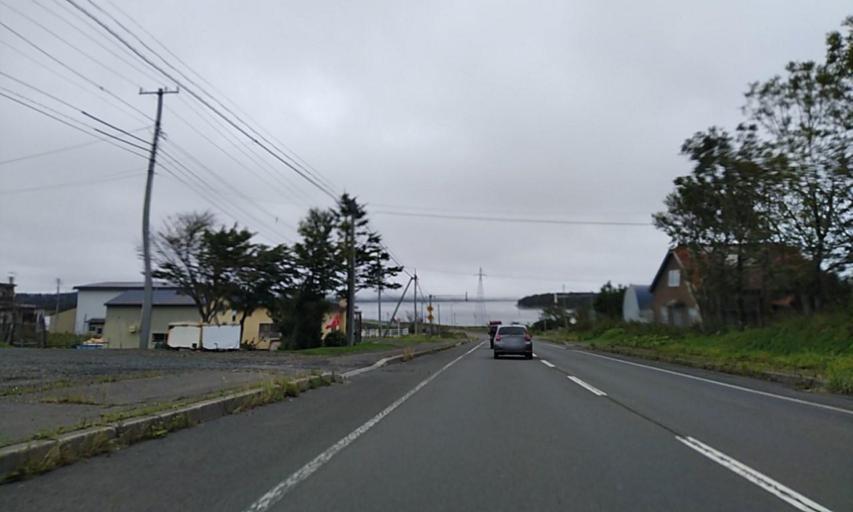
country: JP
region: Hokkaido
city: Nemuro
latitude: 43.2676
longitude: 145.4827
